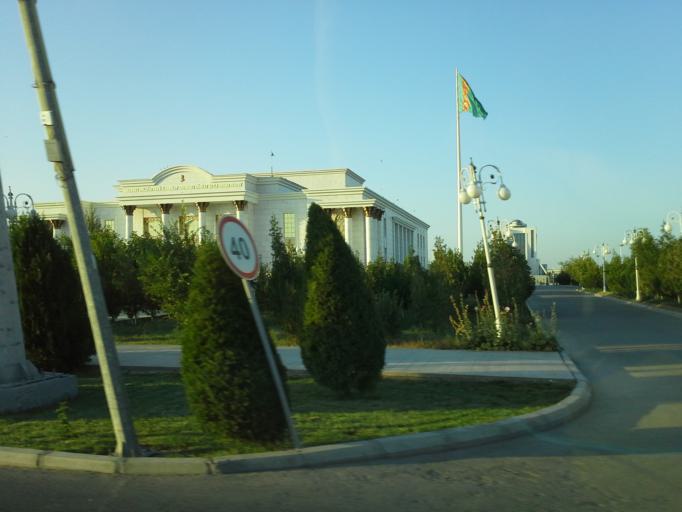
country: TM
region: Dasoguz
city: Dasoguz
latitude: 41.8244
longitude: 59.9633
